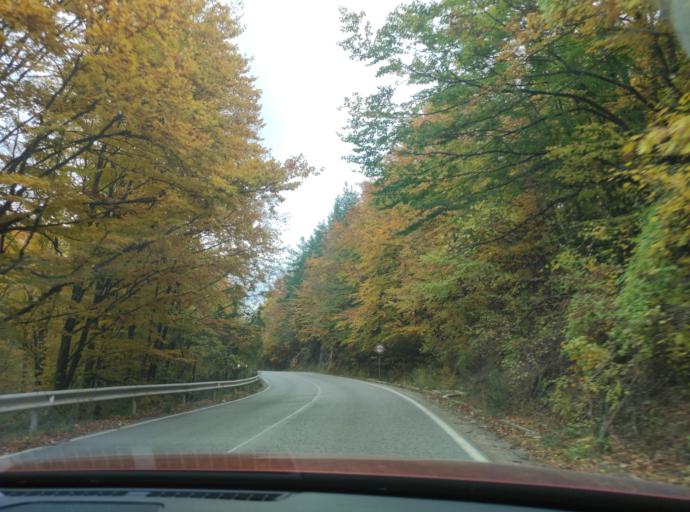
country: BG
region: Sofiya
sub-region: Obshtina Godech
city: Godech
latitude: 43.0203
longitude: 23.1312
